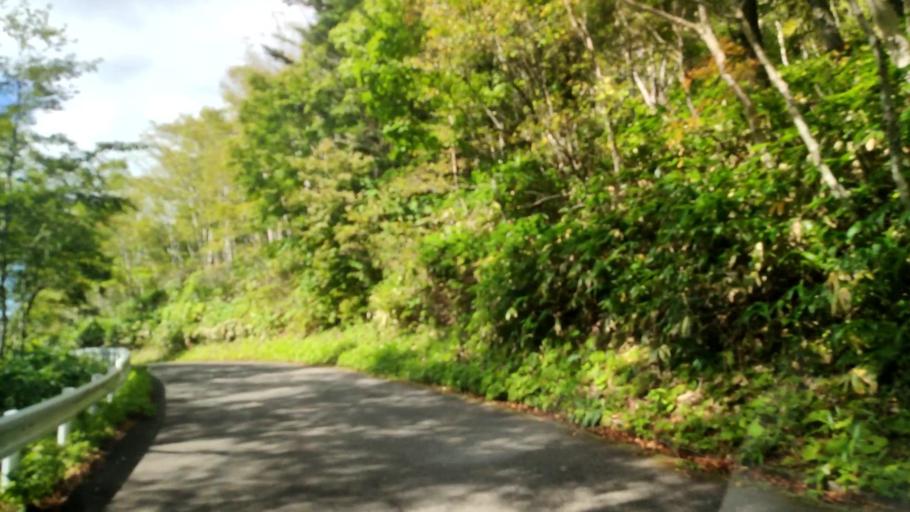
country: JP
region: Gunma
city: Nakanojomachi
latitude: 36.7084
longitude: 138.6556
